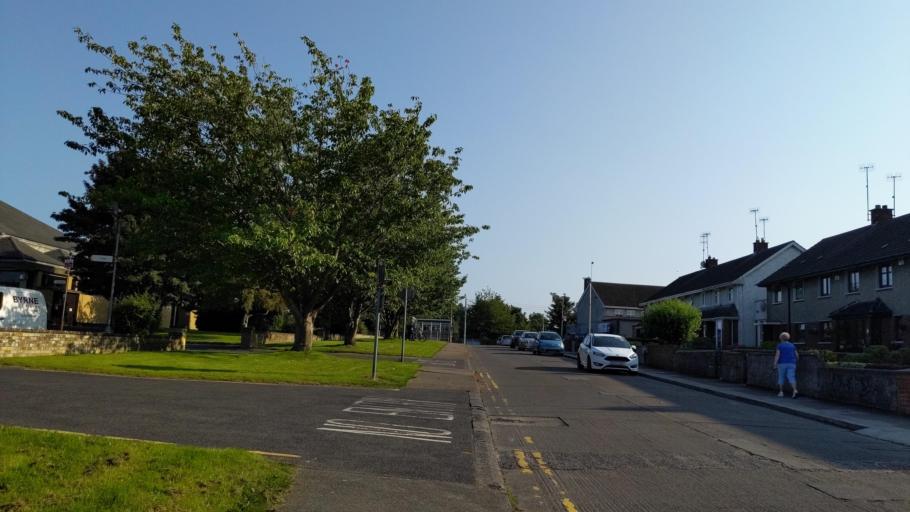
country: IE
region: Leinster
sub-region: Lu
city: Drogheda
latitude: 53.7128
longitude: -6.3605
